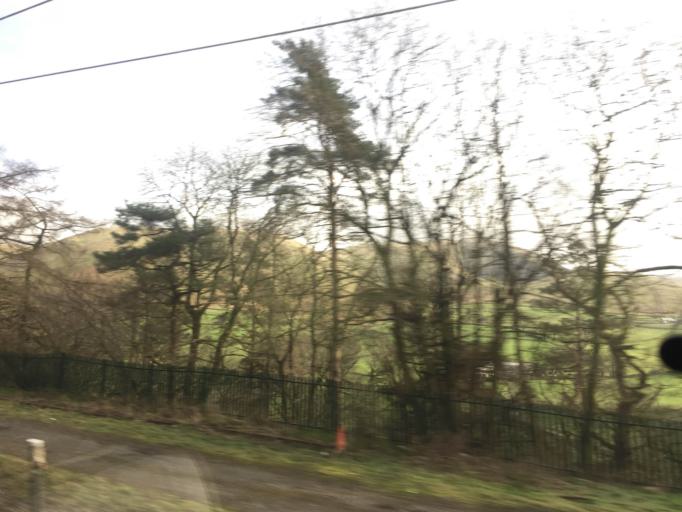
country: GB
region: England
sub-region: Cumbria
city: Sedbergh
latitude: 54.3713
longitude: -2.5824
